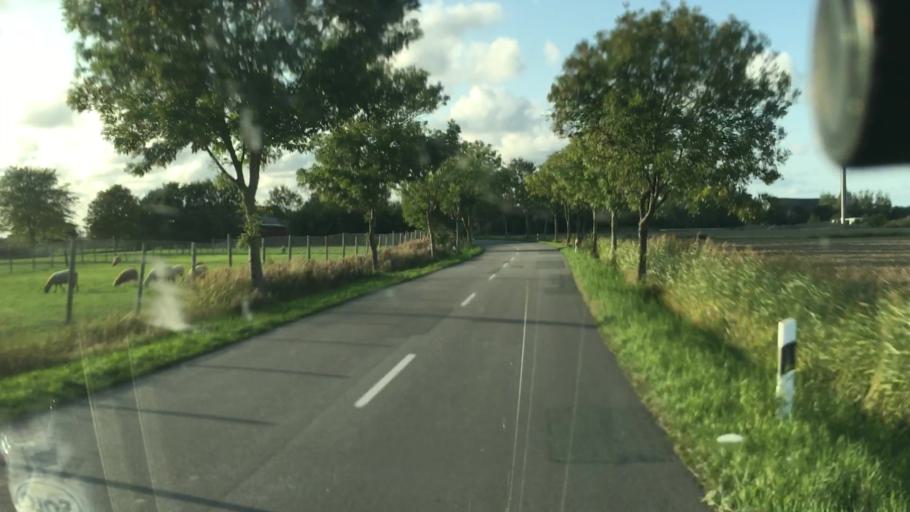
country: DE
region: Lower Saxony
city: Neuharlingersiel
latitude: 53.6843
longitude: 7.7026
